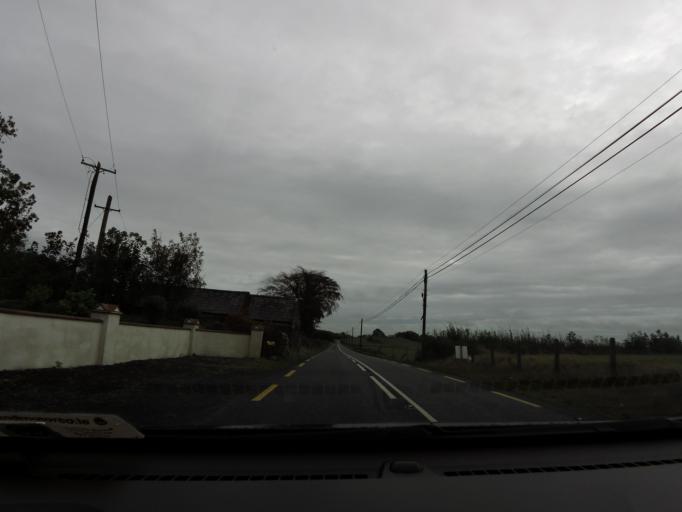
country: IE
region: Connaught
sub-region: County Galway
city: Tuam
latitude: 53.5956
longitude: -8.7688
